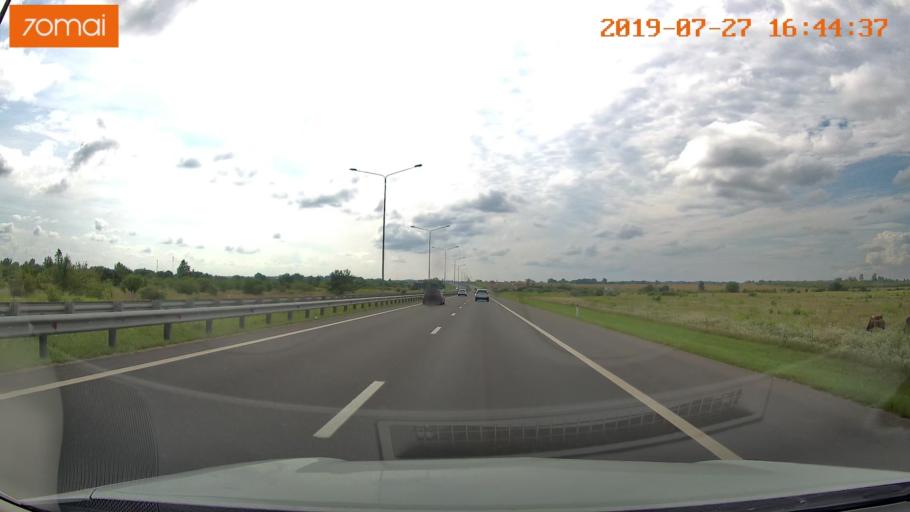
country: RU
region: Kaliningrad
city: Gvardeysk
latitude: 54.6721
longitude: 21.0717
